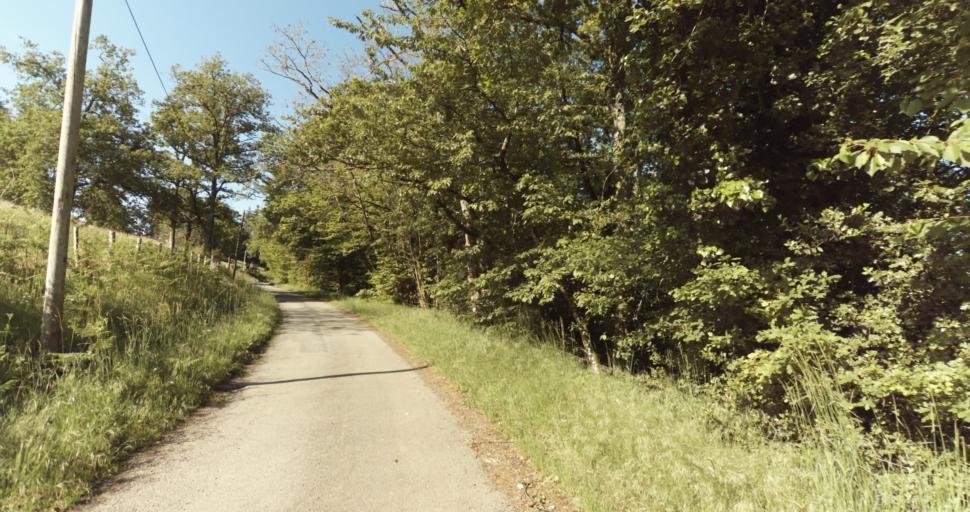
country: FR
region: Limousin
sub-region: Departement de la Haute-Vienne
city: Solignac
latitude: 45.7342
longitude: 1.2436
